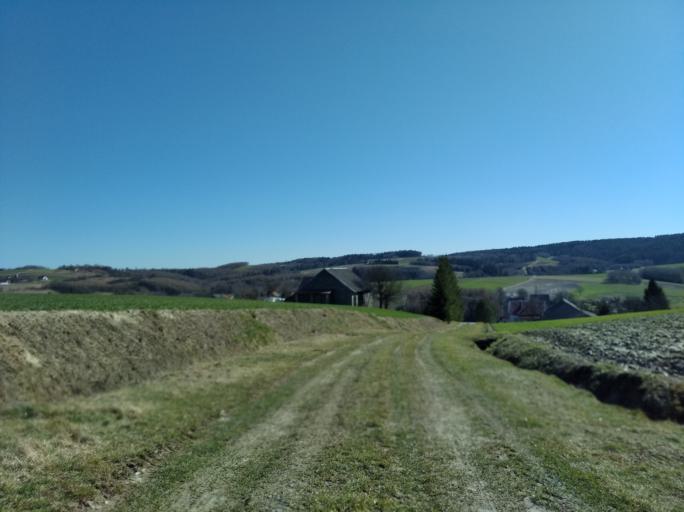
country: PL
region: Subcarpathian Voivodeship
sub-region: Powiat strzyzowski
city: Wisniowa
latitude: 49.9134
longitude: 21.6864
